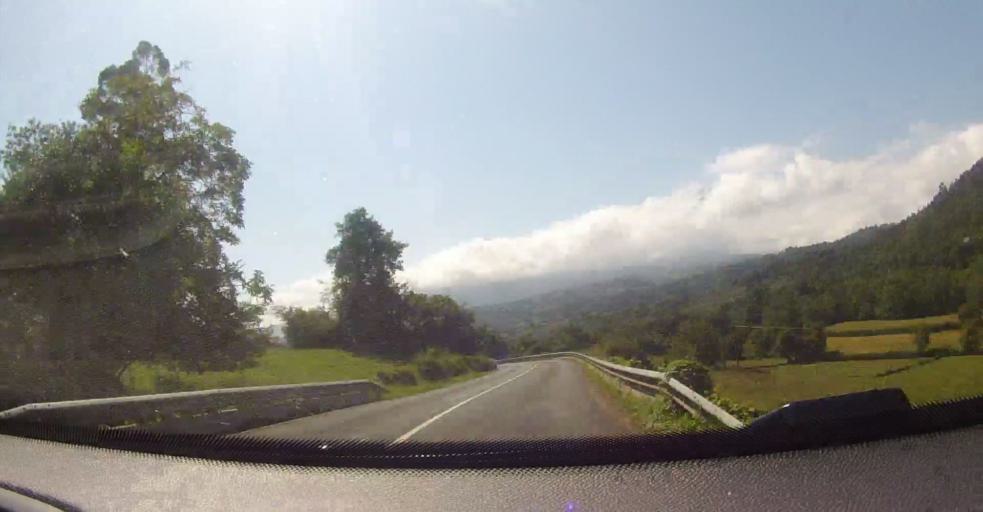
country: ES
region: Asturias
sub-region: Province of Asturias
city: Colunga
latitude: 43.4904
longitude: -5.3120
